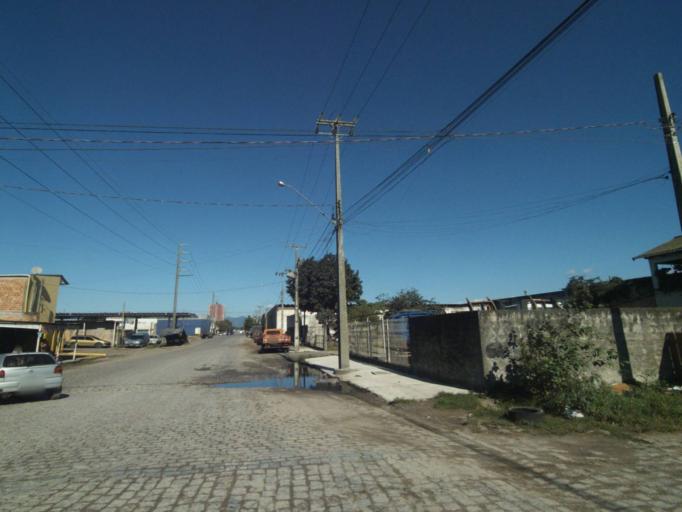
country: BR
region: Parana
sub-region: Paranagua
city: Paranagua
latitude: -25.5120
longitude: -48.5118
